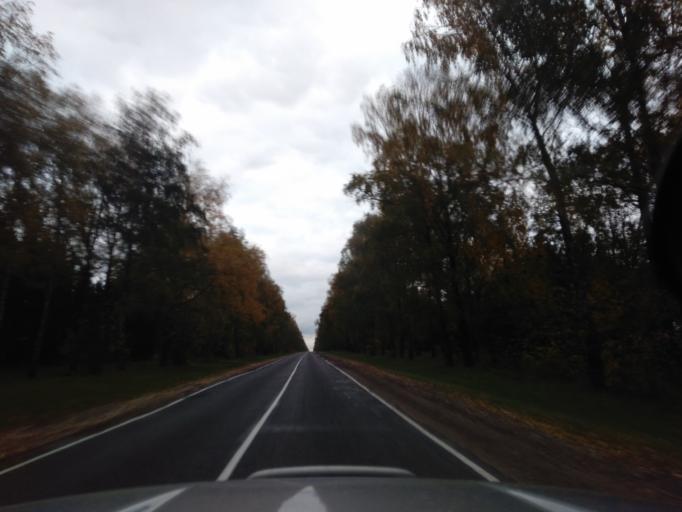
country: BY
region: Minsk
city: Slutsk
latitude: 53.2173
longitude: 27.4225
